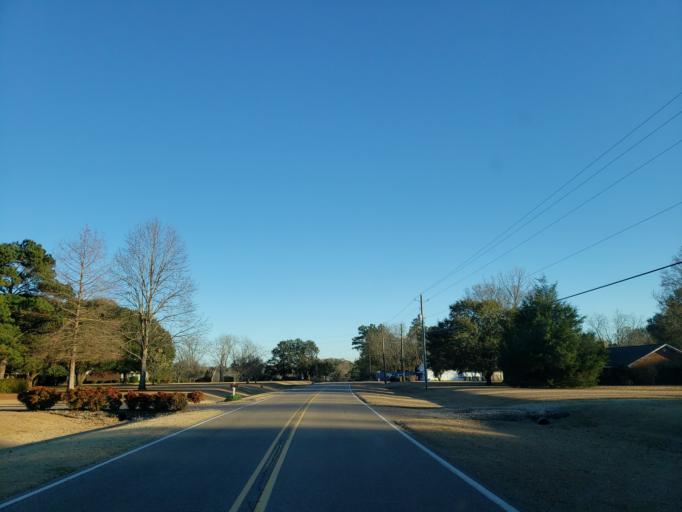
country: US
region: Mississippi
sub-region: Forrest County
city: Rawls Springs
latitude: 31.4317
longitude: -89.3619
